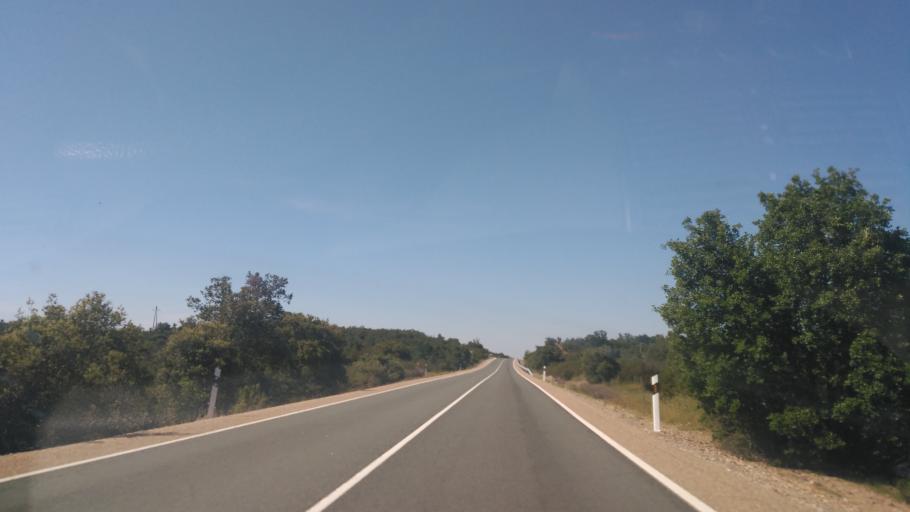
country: ES
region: Castille and Leon
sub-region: Provincia de Zamora
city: Corrales
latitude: 41.2935
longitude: -5.7241
